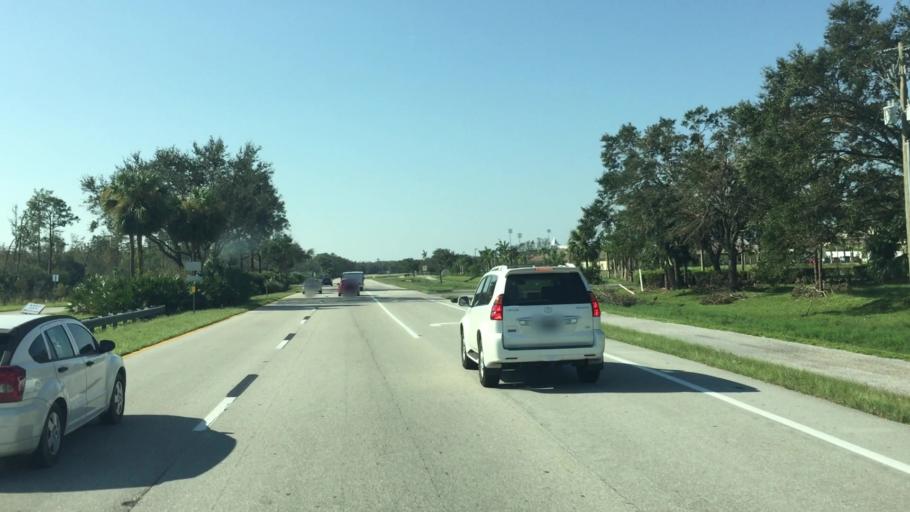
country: US
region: Florida
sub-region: Lee County
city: Villas
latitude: 26.5453
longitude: -81.8395
